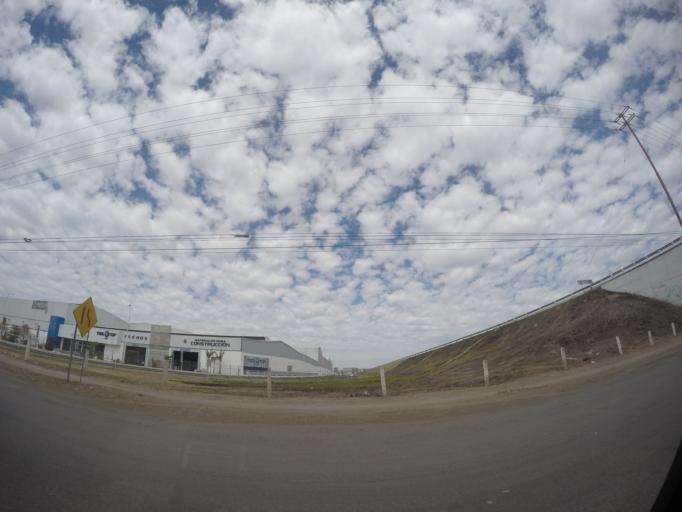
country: MX
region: Guanajuato
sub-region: Leon
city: San Jose de Duran (Los Troncoso)
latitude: 21.0716
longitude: -101.6831
